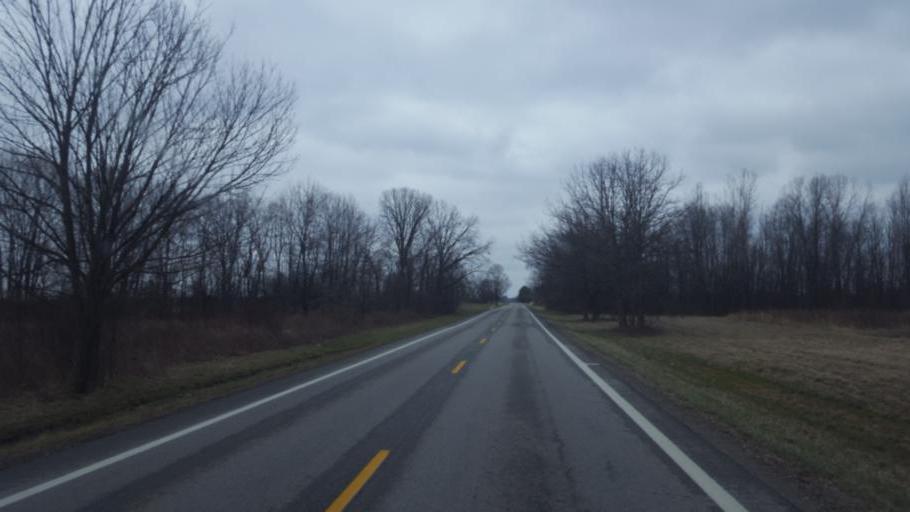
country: US
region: Ohio
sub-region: Delaware County
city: Ashley
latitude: 40.4307
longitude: -83.0440
